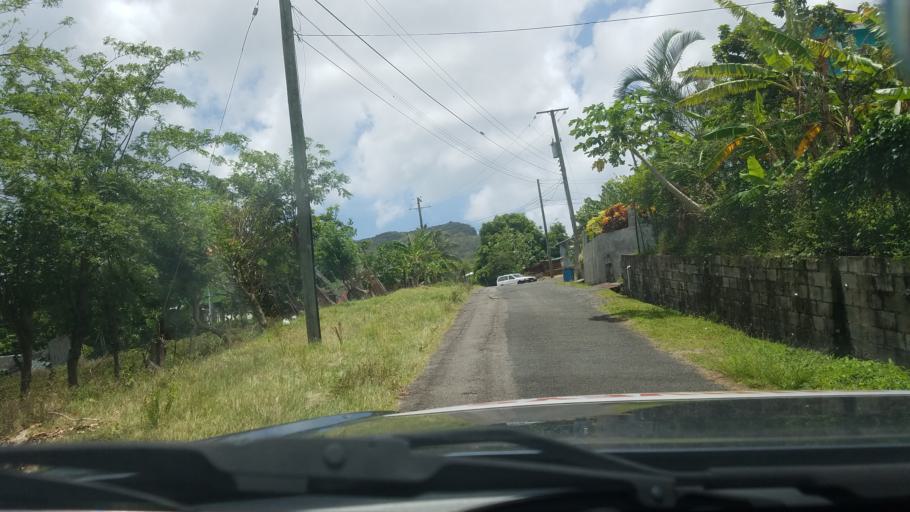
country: LC
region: Gros-Islet
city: Gros Islet
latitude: 14.0564
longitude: -60.9289
